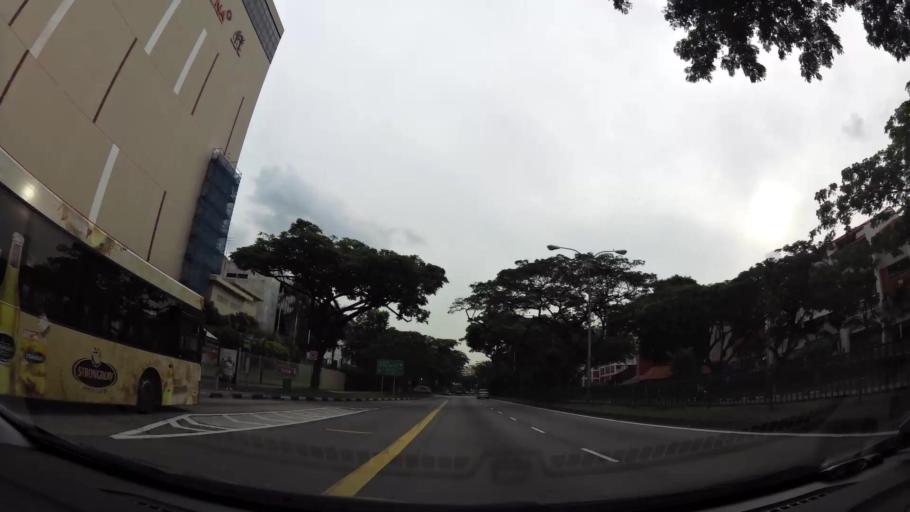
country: SG
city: Singapore
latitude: 1.3540
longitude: 103.8914
